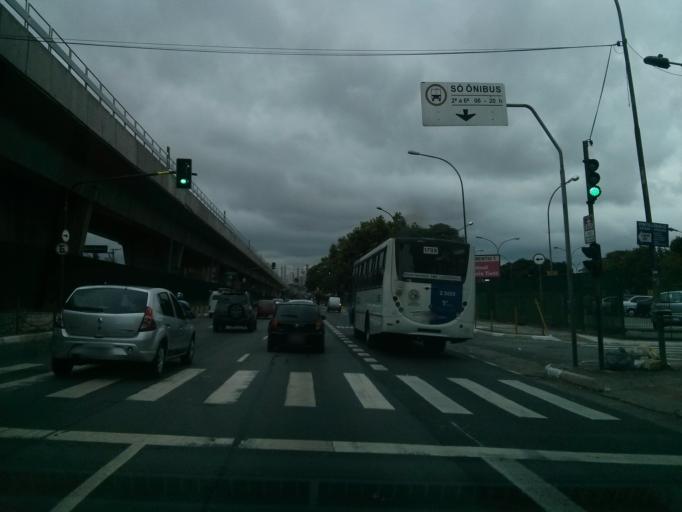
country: BR
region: Sao Paulo
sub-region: Sao Paulo
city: Sao Paulo
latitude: -23.5154
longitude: -46.6249
